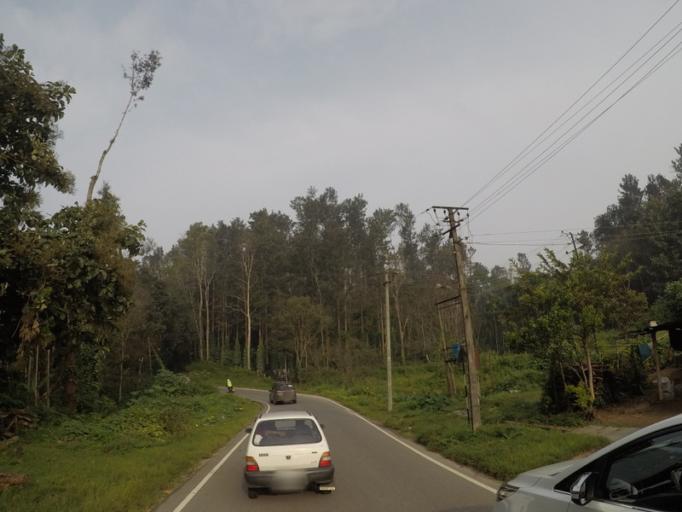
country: IN
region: Karnataka
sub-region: Chikmagalur
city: Mudigere
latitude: 13.2600
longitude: 75.6337
